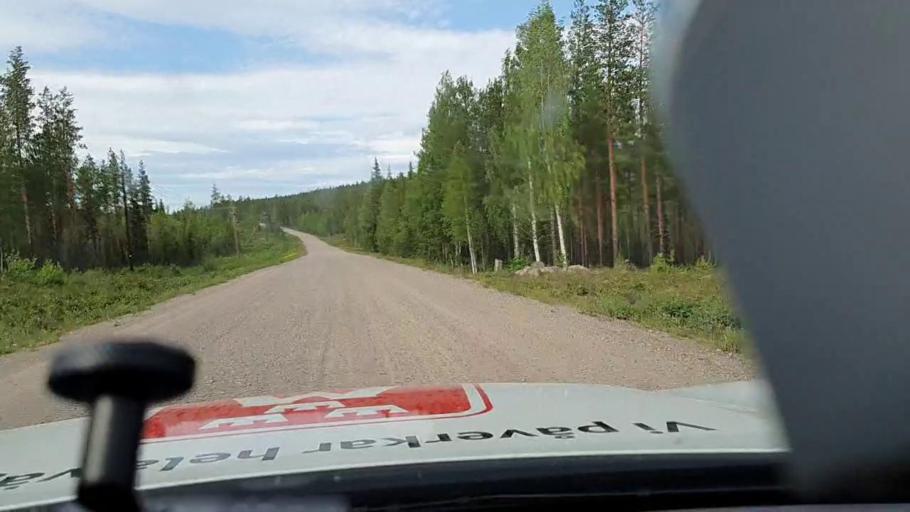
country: SE
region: Norrbotten
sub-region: Alvsbyns Kommun
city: AElvsbyn
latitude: 66.1260
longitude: 20.9961
